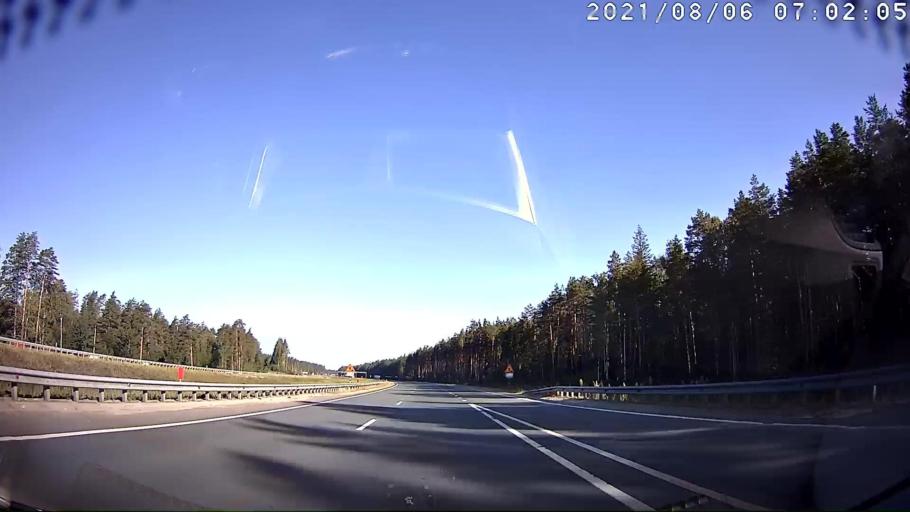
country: RU
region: Mariy-El
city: Surok
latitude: 56.5307
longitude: 48.0023
